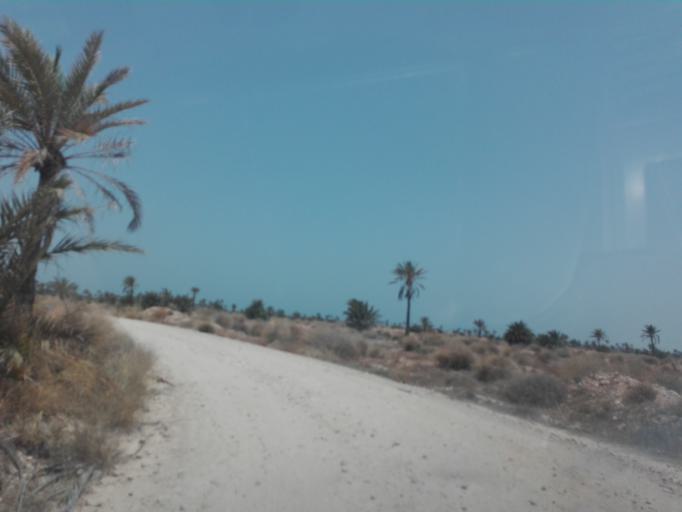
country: TN
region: Safaqis
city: Al Qarmadah
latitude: 34.6600
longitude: 11.0996
